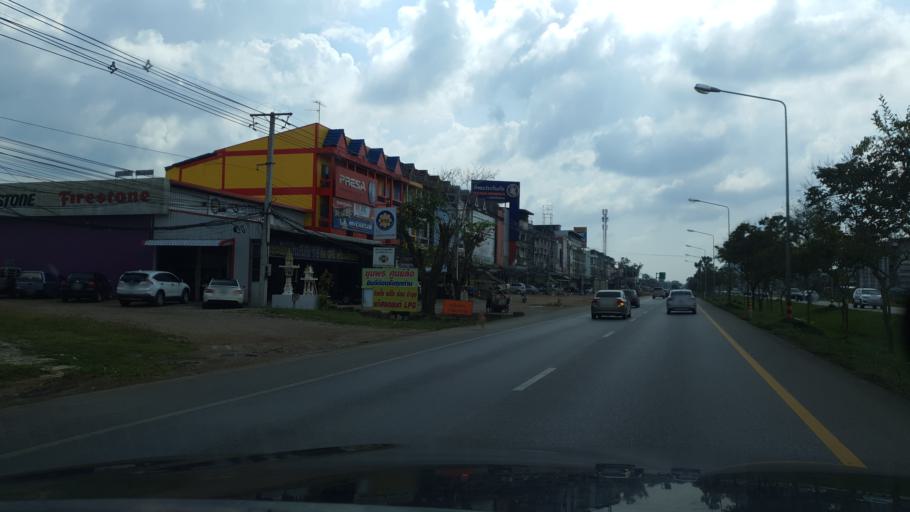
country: TH
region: Chumphon
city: Chumphon
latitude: 10.4905
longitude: 99.1224
